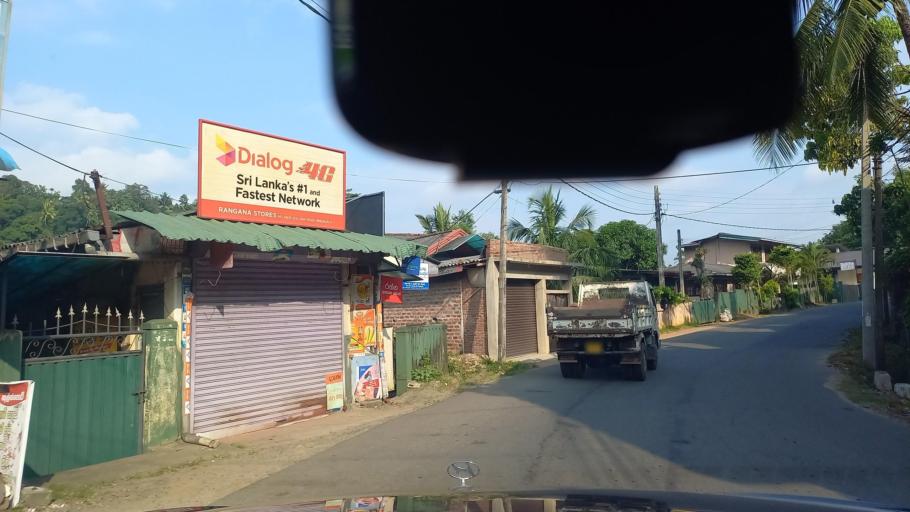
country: LK
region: Central
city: Kandy
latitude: 7.2376
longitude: 80.6013
